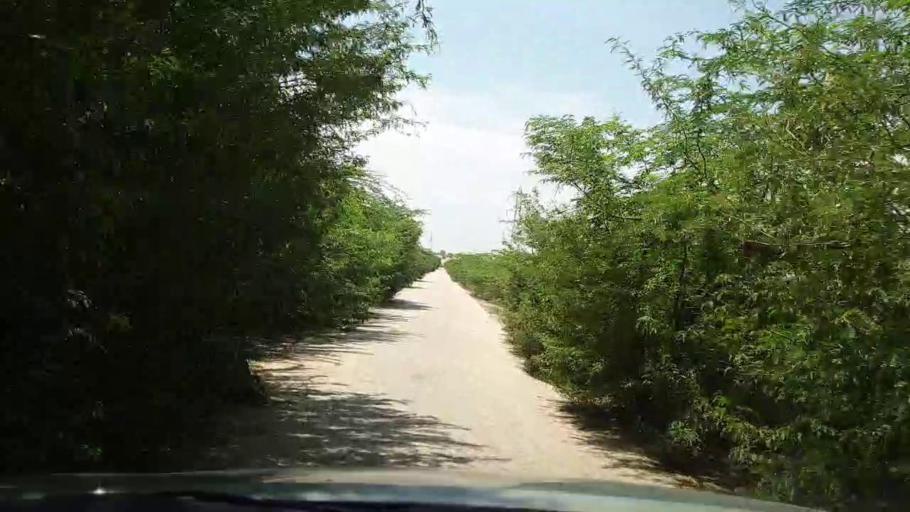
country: PK
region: Sindh
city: Bozdar
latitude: 27.0838
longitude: 68.9662
